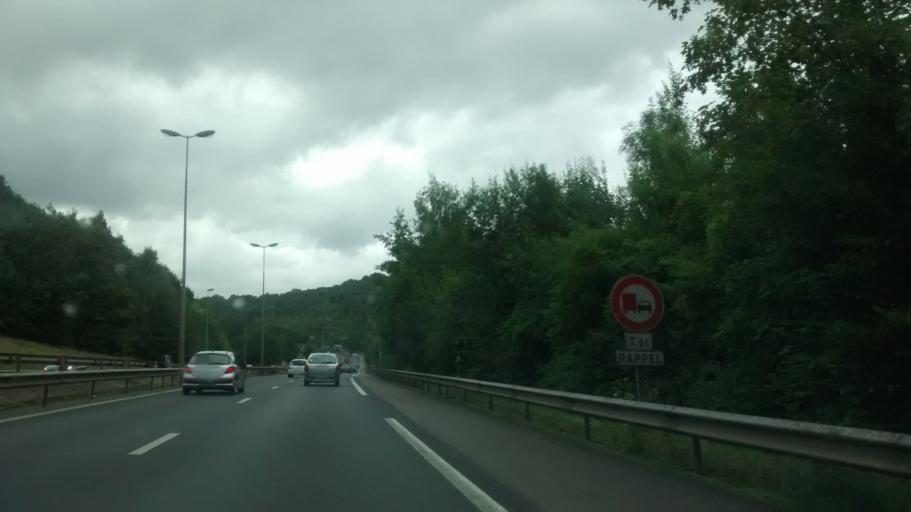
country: FR
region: Haute-Normandie
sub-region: Departement de la Seine-Maritime
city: Darnetal
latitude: 49.4540
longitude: 1.1448
